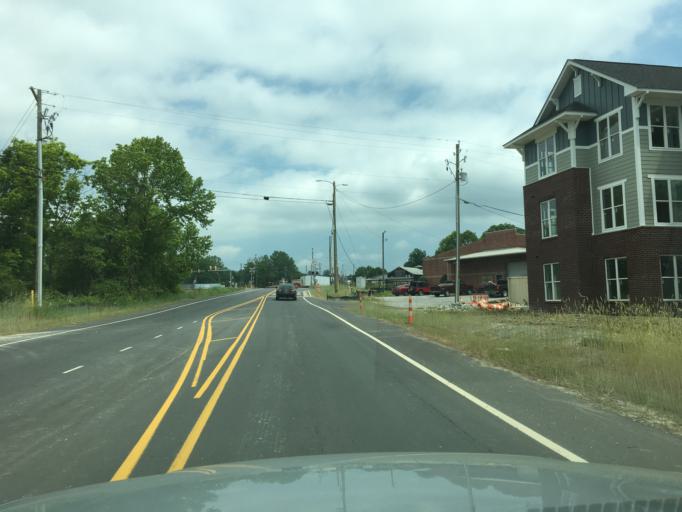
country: US
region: North Carolina
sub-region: Henderson County
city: Fletcher
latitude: 35.4265
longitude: -82.5011
